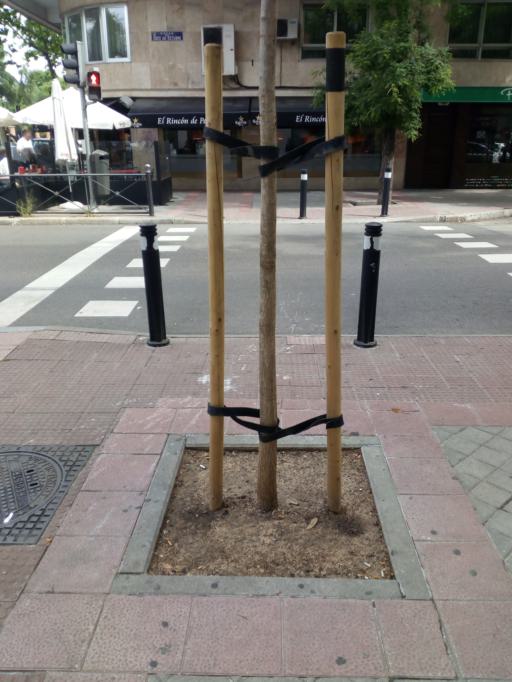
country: ES
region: Madrid
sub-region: Provincia de Madrid
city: Retiro
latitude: 40.4156
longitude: -3.6776
